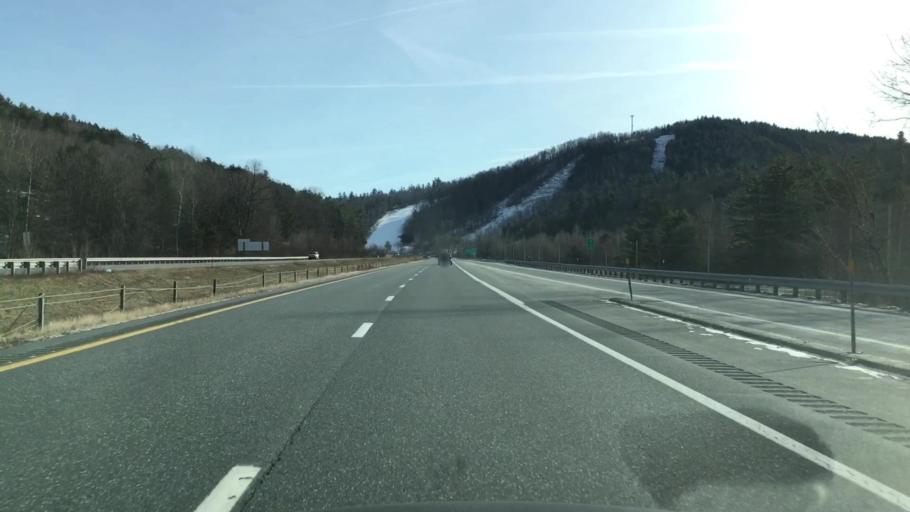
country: US
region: New Hampshire
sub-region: Grafton County
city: Enfield
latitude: 43.6087
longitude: -72.1873
